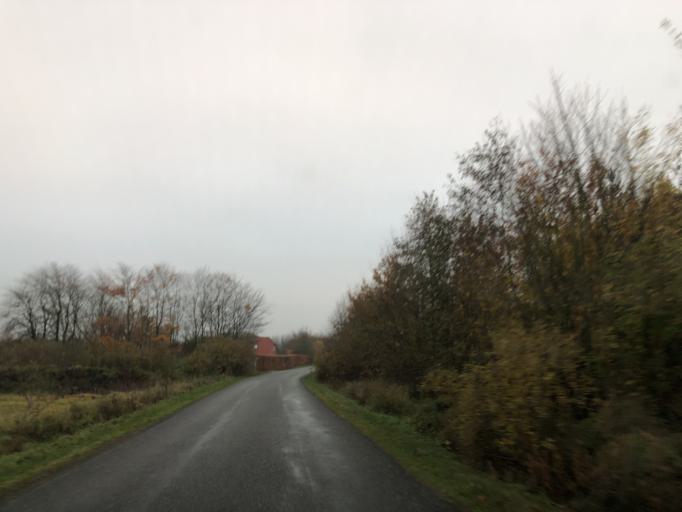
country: DK
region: Central Jutland
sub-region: Herning Kommune
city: Vildbjerg
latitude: 56.2046
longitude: 8.7077
